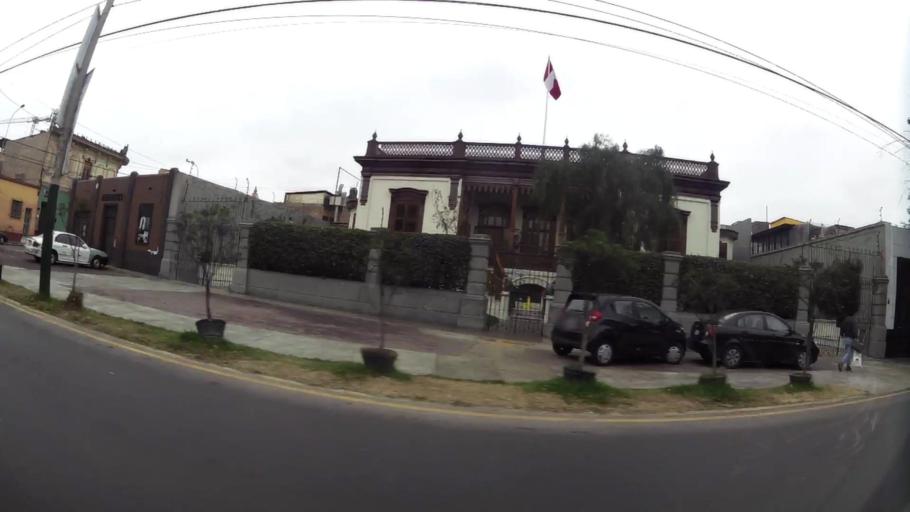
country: PE
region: Lima
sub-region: Lima
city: Surco
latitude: -12.1473
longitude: -77.0224
